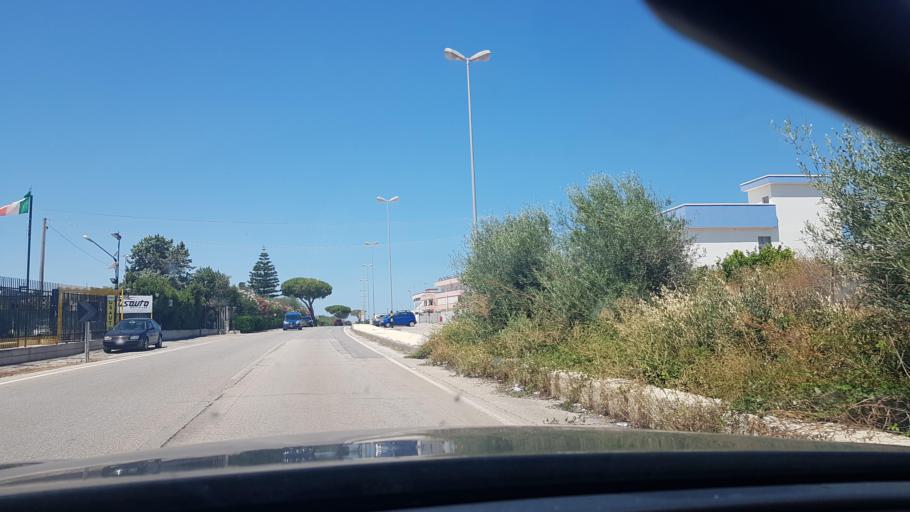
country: IT
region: Apulia
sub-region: Provincia di Barletta - Andria - Trani
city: Barletta
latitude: 41.3034
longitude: 16.3219
